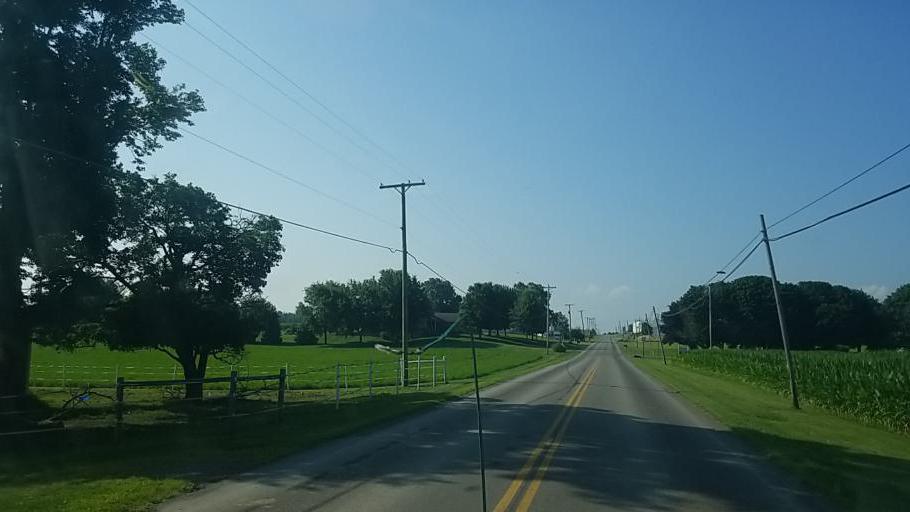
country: US
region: Ohio
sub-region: Wayne County
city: Dalton
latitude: 40.7325
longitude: -81.7451
